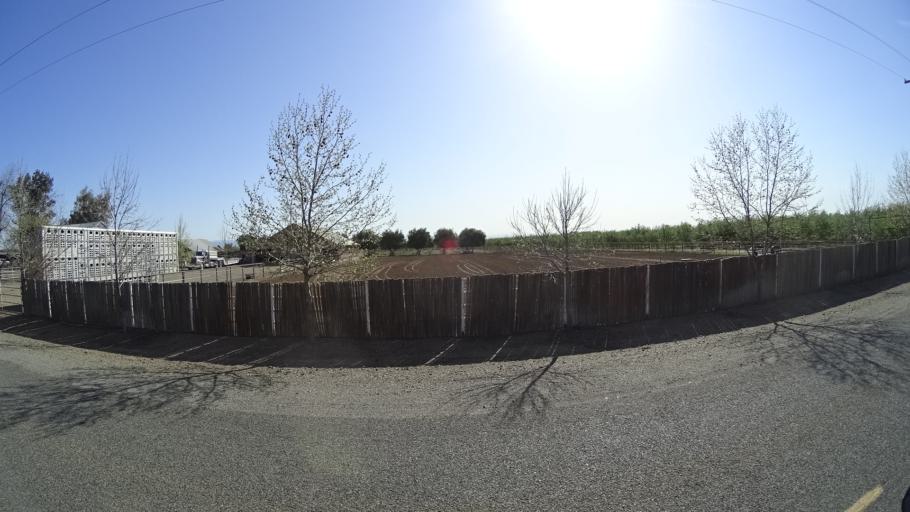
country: US
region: California
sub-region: Glenn County
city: Hamilton City
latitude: 39.7880
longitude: -122.0853
